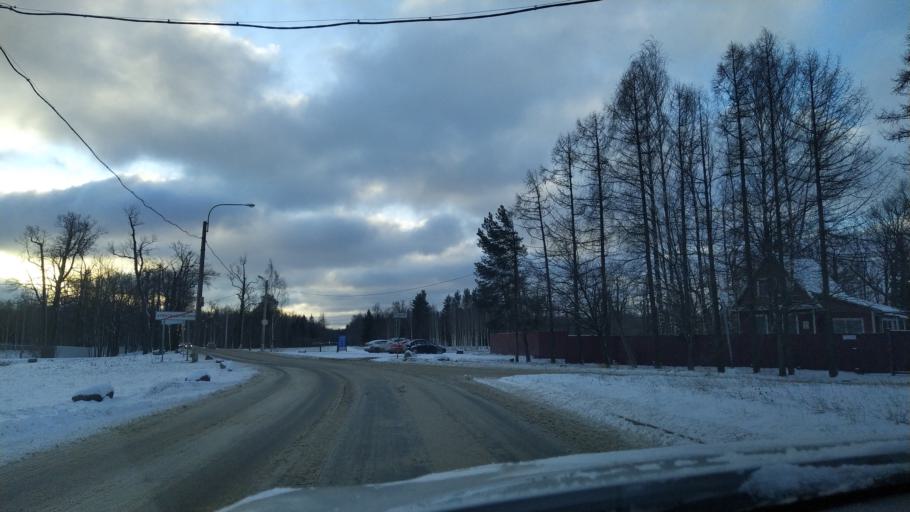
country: RU
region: St.-Petersburg
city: Aleksandrovskaya
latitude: 59.7283
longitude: 30.3559
